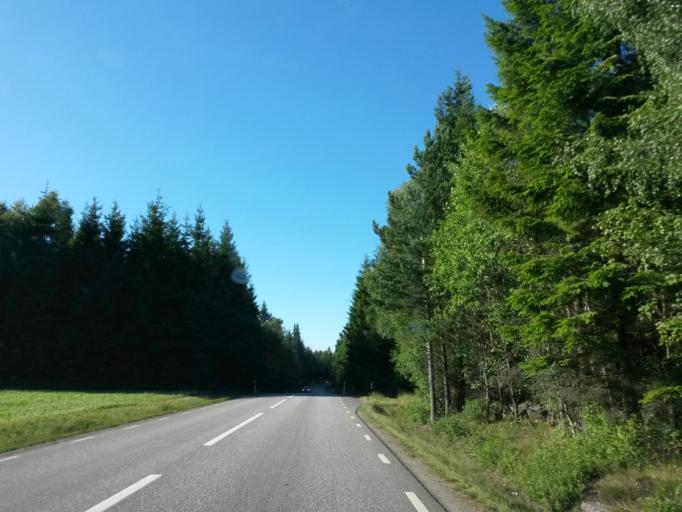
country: SE
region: Vaestra Goetaland
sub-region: Boras Kommun
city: Boras
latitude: 57.8790
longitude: 12.9289
